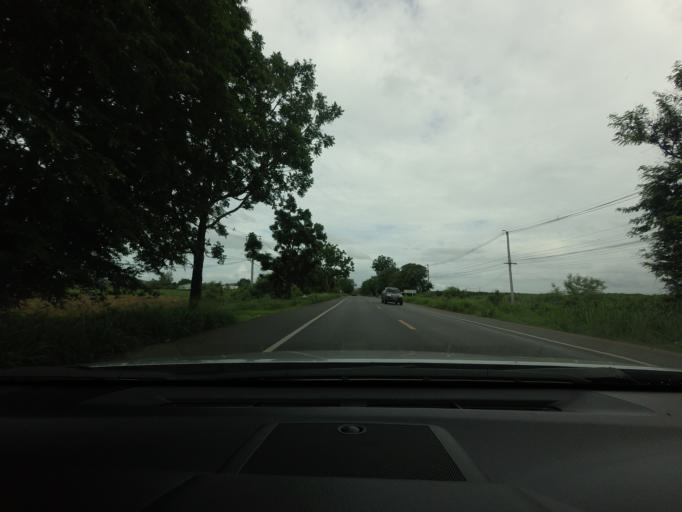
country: TH
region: Prachuap Khiri Khan
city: Hua Hin
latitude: 12.5809
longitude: 99.8593
